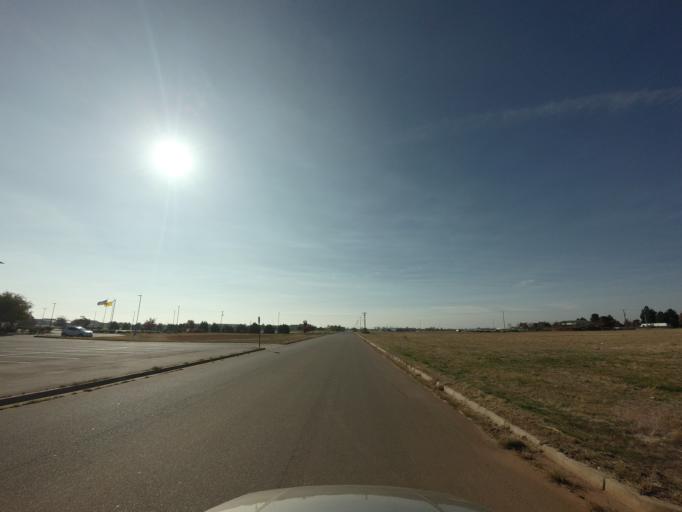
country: US
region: New Mexico
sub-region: Curry County
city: Clovis
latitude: 34.4069
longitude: -103.1683
